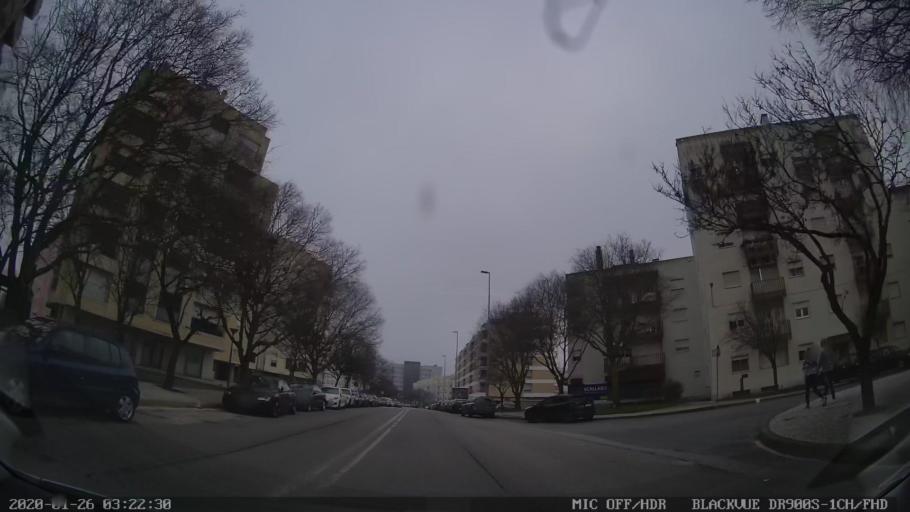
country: PT
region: Santarem
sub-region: Santarem
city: Santarem
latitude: 39.2255
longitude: -8.6904
